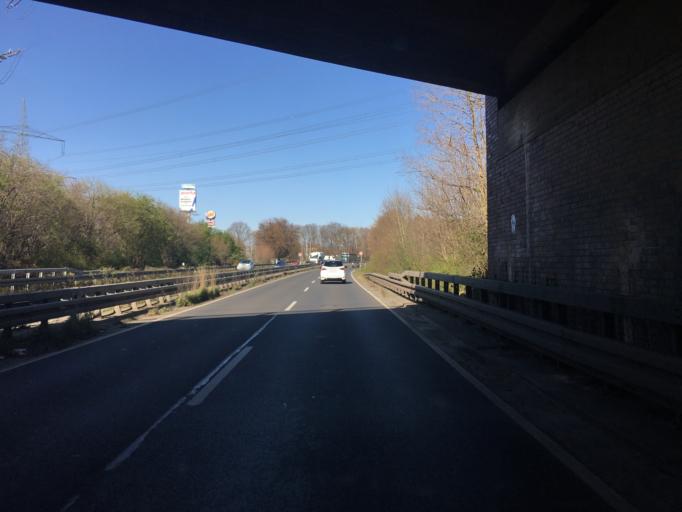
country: DE
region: North Rhine-Westphalia
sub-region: Regierungsbezirk Koln
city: Frechen
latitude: 50.9135
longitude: 6.8364
